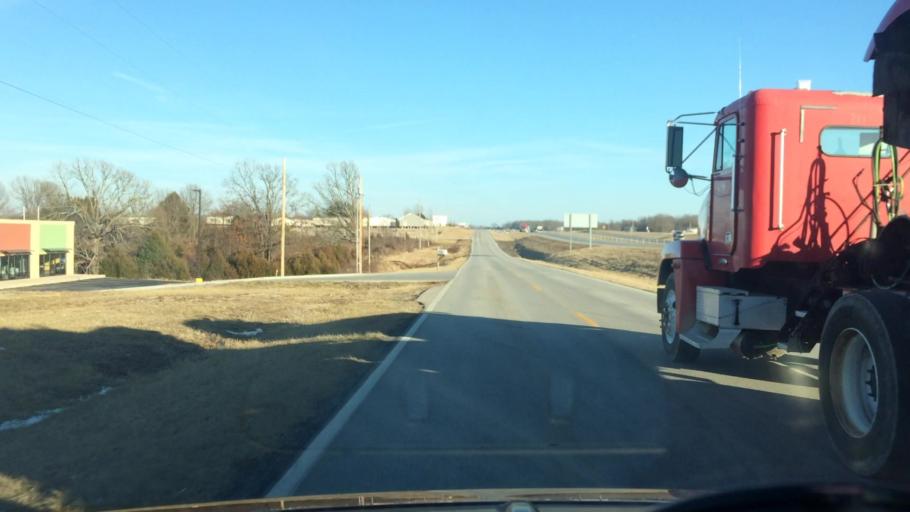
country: US
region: Missouri
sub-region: Greene County
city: Strafford
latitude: 37.2708
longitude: -93.0872
